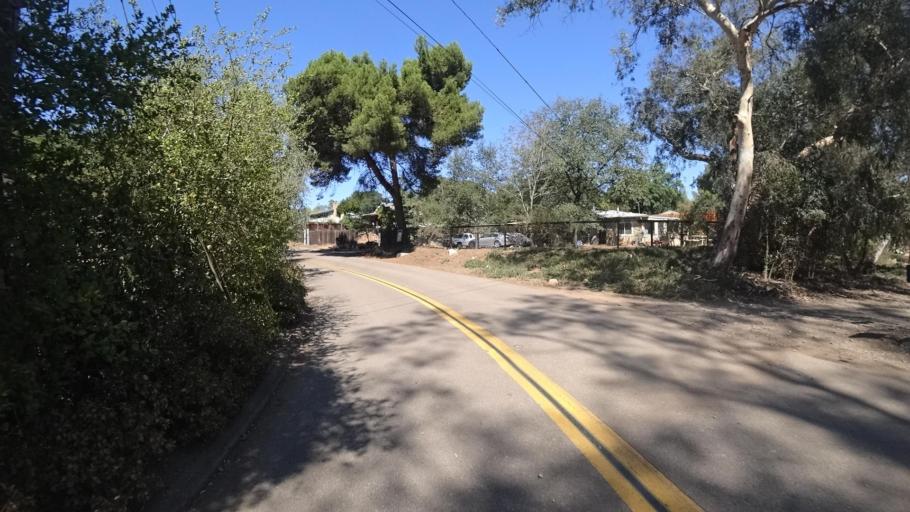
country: US
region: California
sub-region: San Diego County
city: Crest
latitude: 32.8012
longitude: -116.8675
